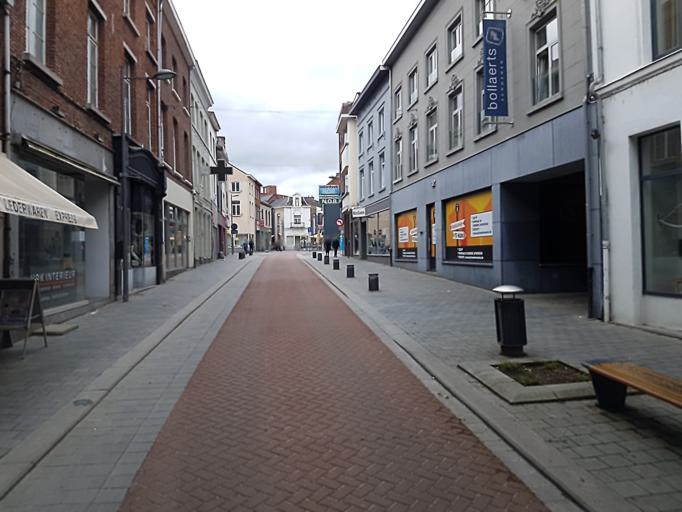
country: BE
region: Flanders
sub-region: Provincie Vlaams-Brabant
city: Tienen
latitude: 50.8094
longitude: 4.9334
